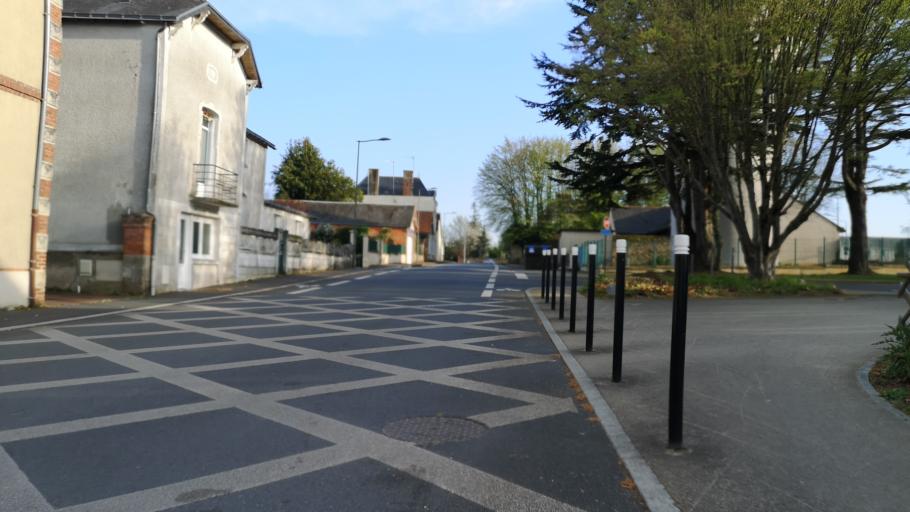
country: FR
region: Pays de la Loire
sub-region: Departement de Maine-et-Loire
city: Chemille-Melay
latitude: 47.2114
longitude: -0.7268
